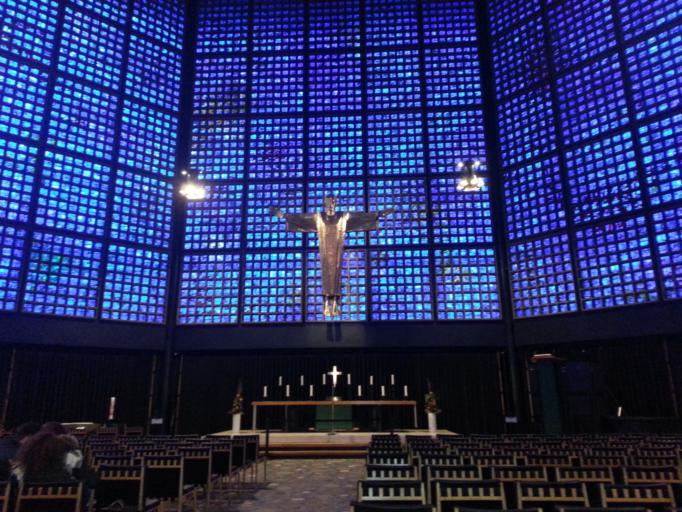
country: DE
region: Berlin
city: Hansaviertel
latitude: 52.5049
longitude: 13.3346
